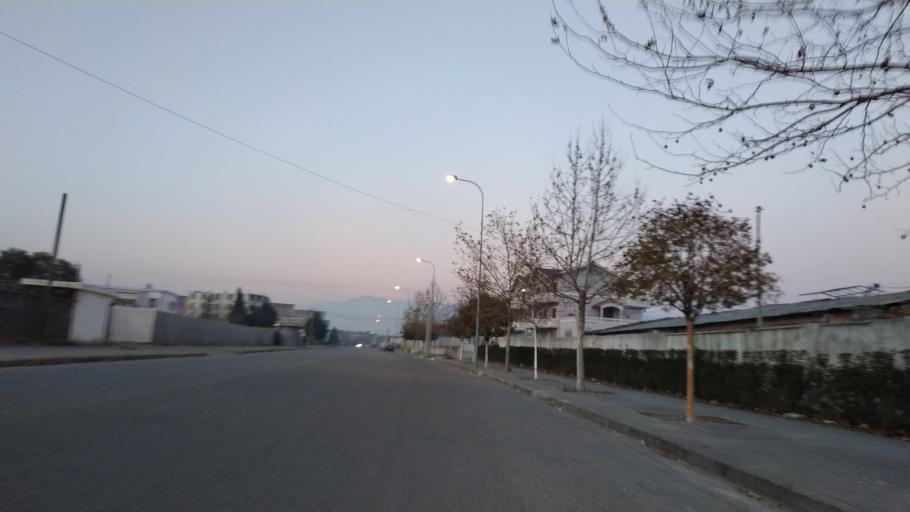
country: AL
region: Shkoder
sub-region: Rrethi i Shkodres
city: Shkoder
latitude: 42.0822
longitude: 19.5299
